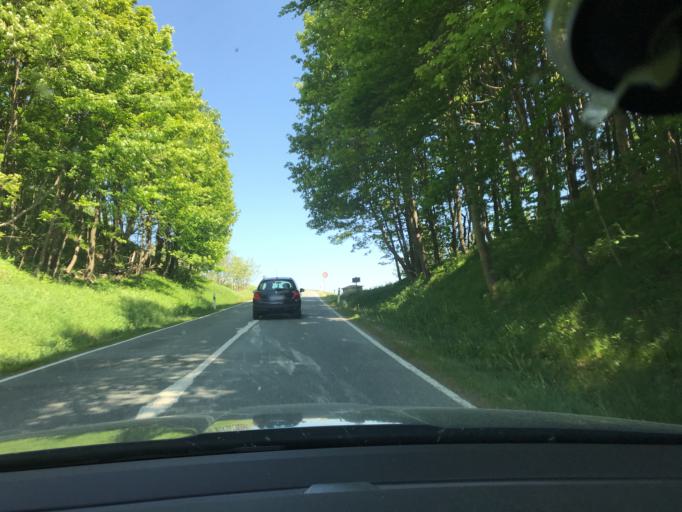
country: CZ
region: Ustecky
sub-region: Okres Chomutov
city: Kovarska
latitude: 50.4495
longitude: 13.0072
